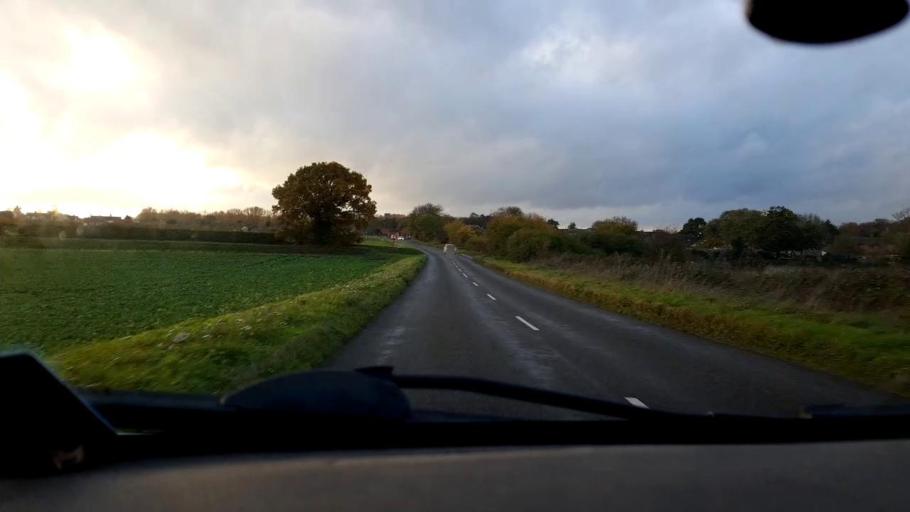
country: GB
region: England
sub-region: Norfolk
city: Spixworth
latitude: 52.6883
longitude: 1.2874
